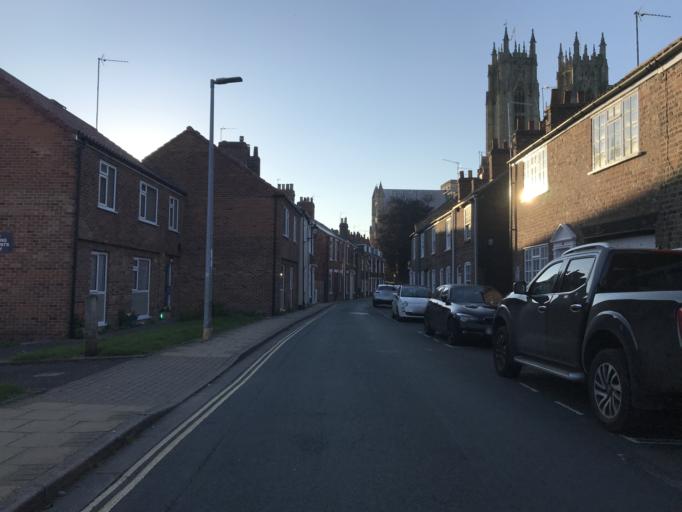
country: GB
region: England
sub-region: East Riding of Yorkshire
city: Beverley
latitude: 53.8393
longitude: -0.4273
